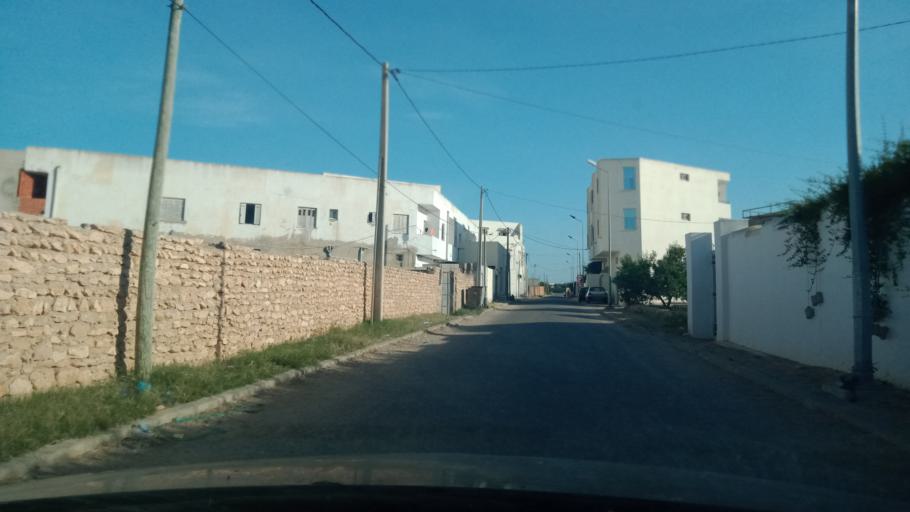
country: TN
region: Safaqis
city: Sfax
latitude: 34.8239
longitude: 10.7357
